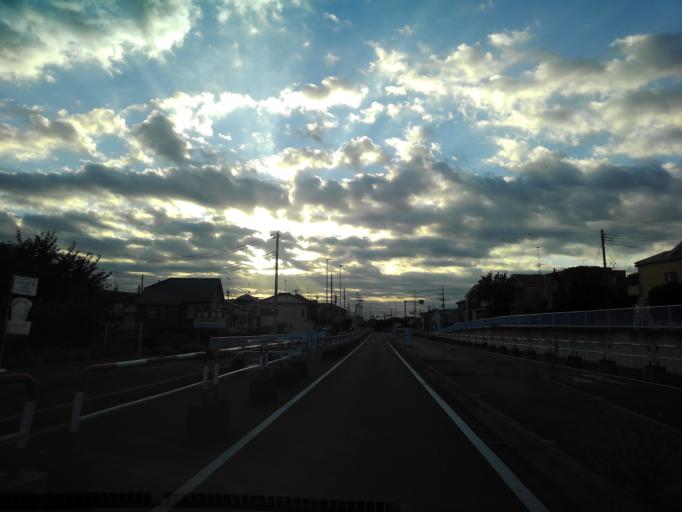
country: JP
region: Saitama
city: Tokorozawa
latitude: 35.7815
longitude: 139.4573
